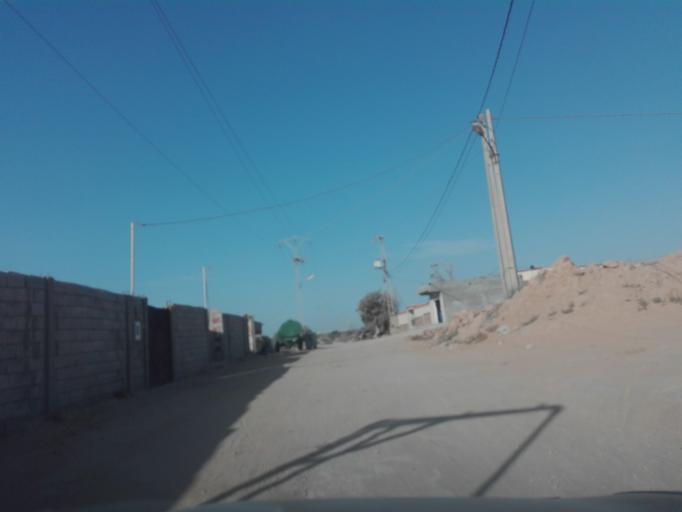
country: TN
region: Qabis
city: Gabes
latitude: 33.9605
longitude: 10.0604
